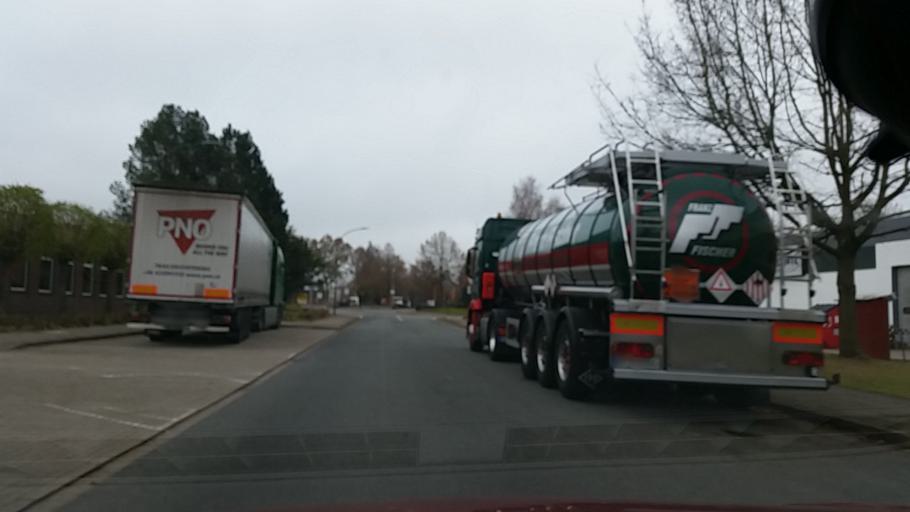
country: DE
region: Schleswig-Holstein
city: Oststeinbek
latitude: 53.5495
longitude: 10.1586
